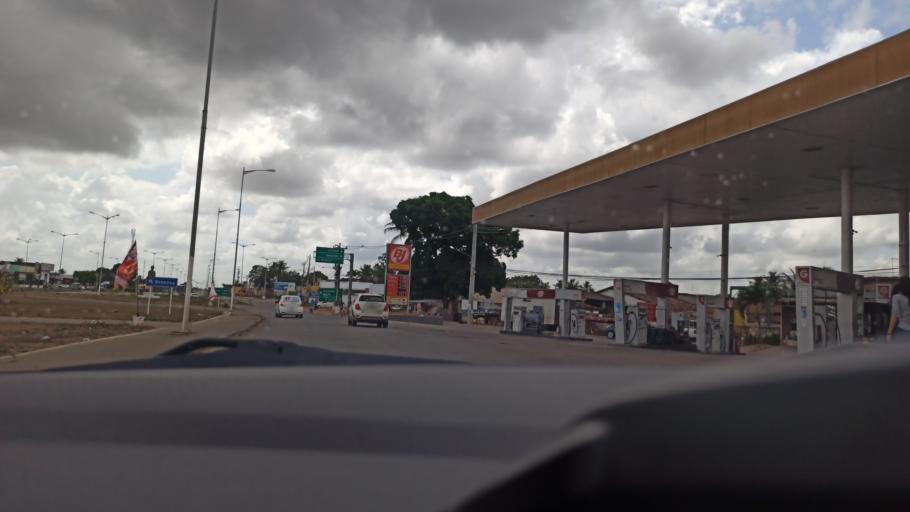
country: BR
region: Pernambuco
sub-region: Carpina
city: Carpina
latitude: -7.8474
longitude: -35.2397
